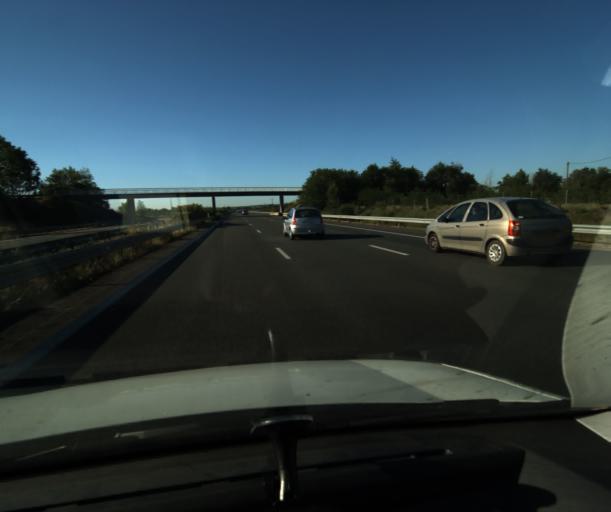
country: FR
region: Midi-Pyrenees
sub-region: Departement du Tarn-et-Garonne
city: Campsas
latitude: 43.8735
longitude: 1.3175
